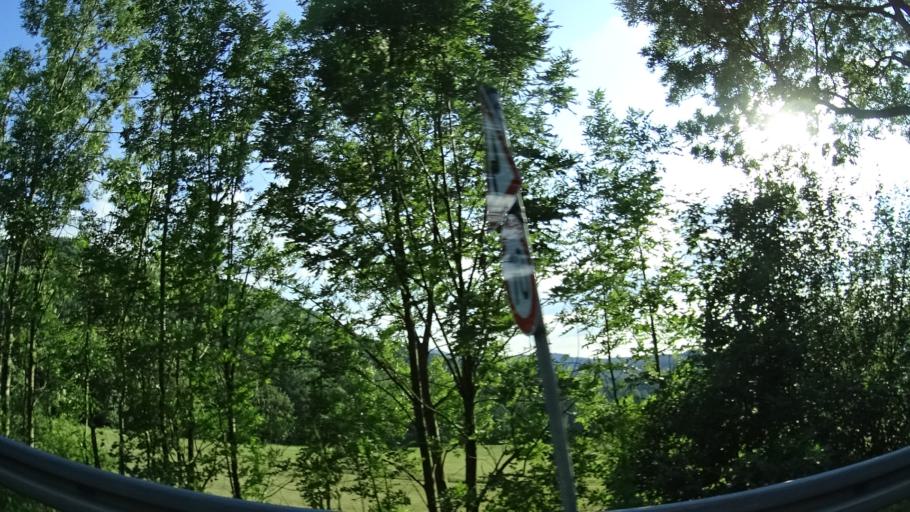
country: DE
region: Hesse
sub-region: Regierungsbezirk Kassel
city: Gersfeld
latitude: 50.4279
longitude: 9.9300
